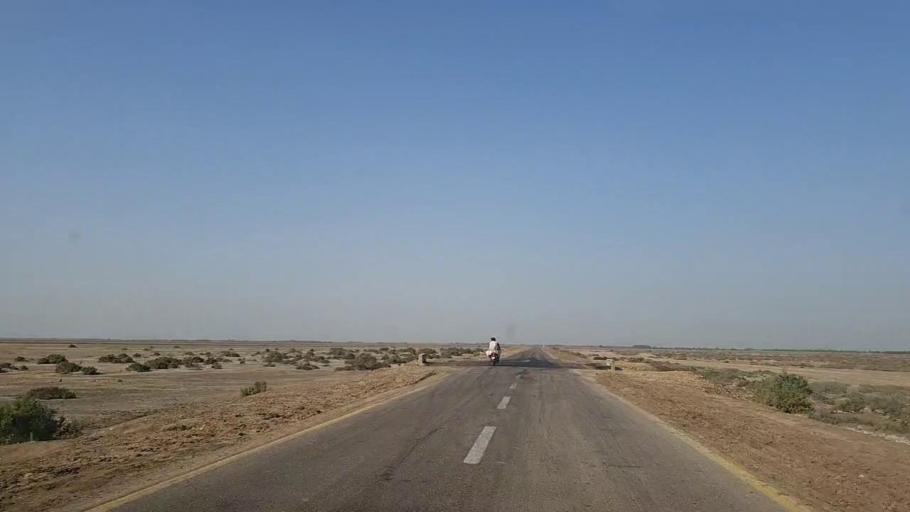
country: PK
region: Sindh
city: Jati
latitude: 24.4907
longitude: 68.3753
